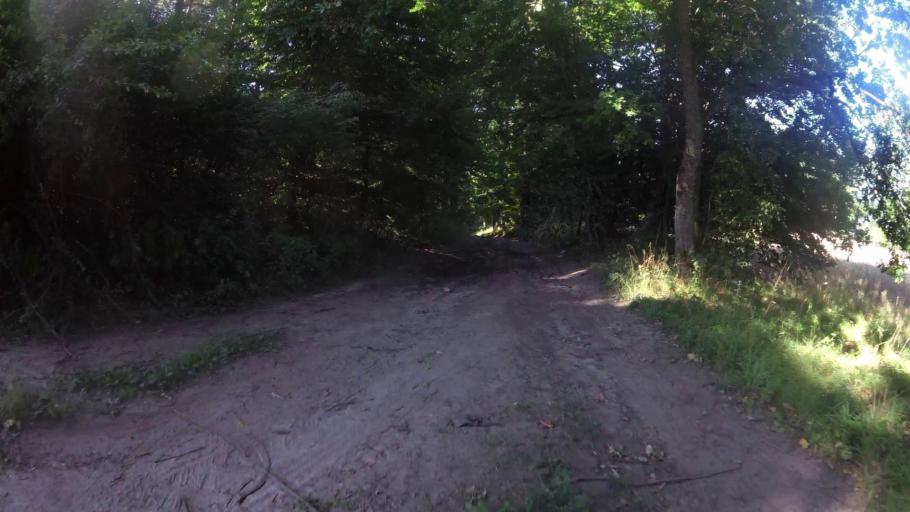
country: PL
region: West Pomeranian Voivodeship
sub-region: Powiat drawski
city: Drawsko Pomorskie
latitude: 53.5355
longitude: 15.7125
